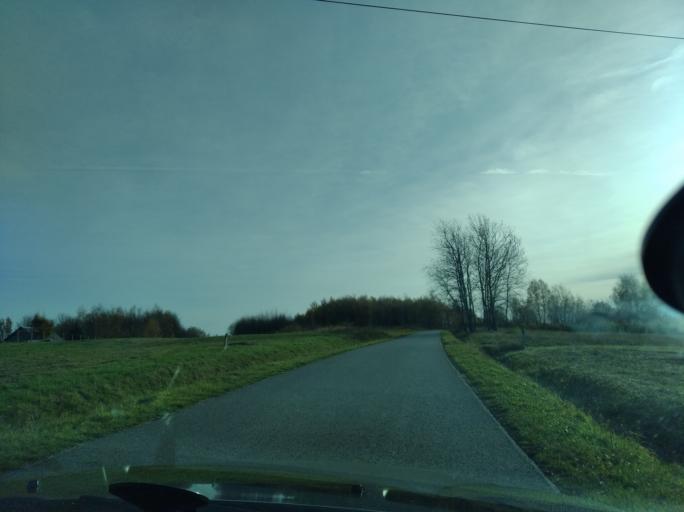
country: PL
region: Subcarpathian Voivodeship
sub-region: Powiat rzeszowski
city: Siedliska
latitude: 49.9366
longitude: 21.9549
